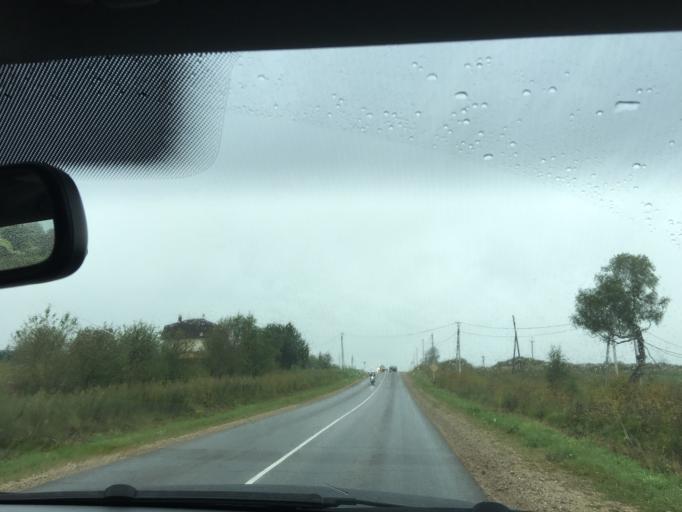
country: RU
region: Kaluga
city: Borovsk
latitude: 55.1666
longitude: 36.4768
